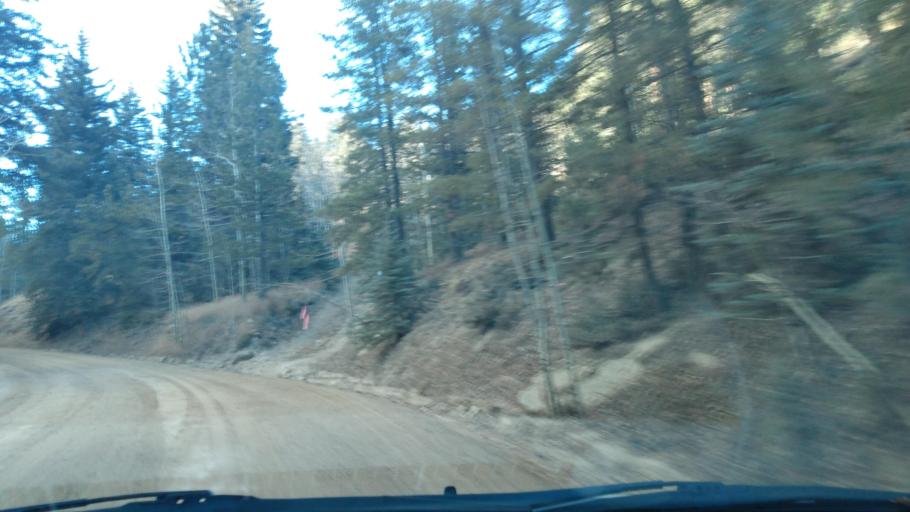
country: US
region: Colorado
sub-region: Boulder County
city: Nederland
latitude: 39.9408
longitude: -105.4416
